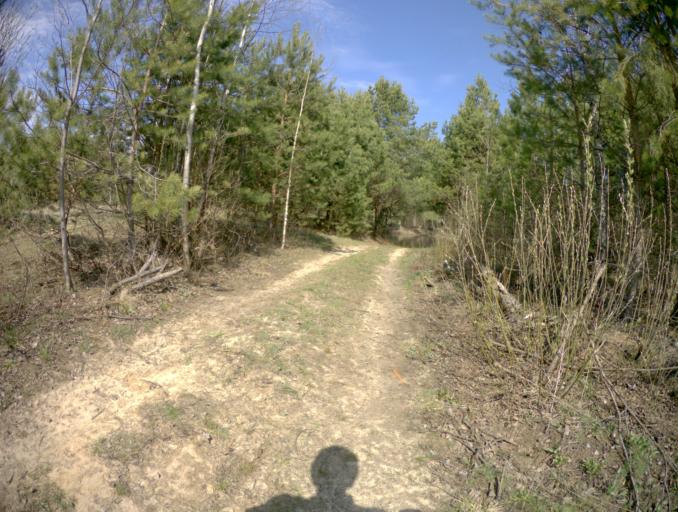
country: RU
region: Vladimir
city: Mezinovskiy
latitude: 55.5431
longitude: 40.2650
